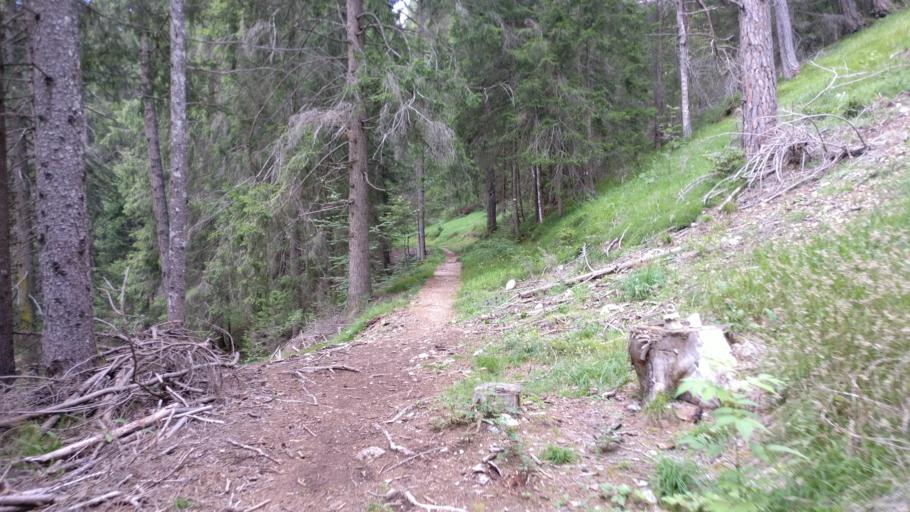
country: IT
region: Trentino-Alto Adige
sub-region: Provincia di Trento
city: Ruffre
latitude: 46.4220
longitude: 11.1940
